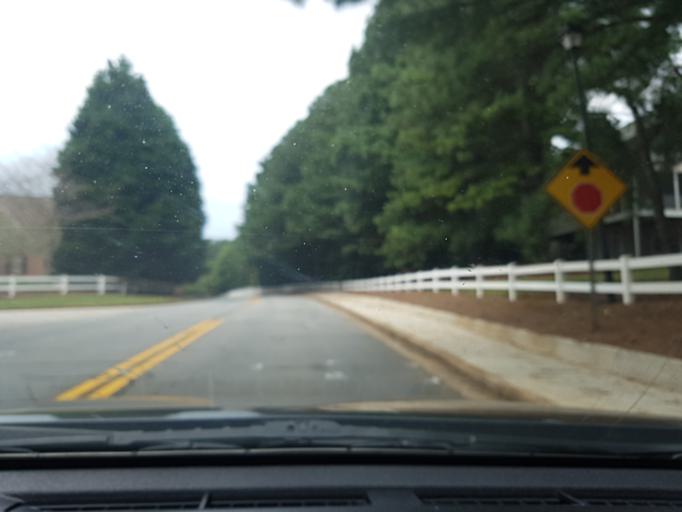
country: US
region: Georgia
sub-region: Gwinnett County
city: Suwanee
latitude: 34.0114
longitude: -84.0378
